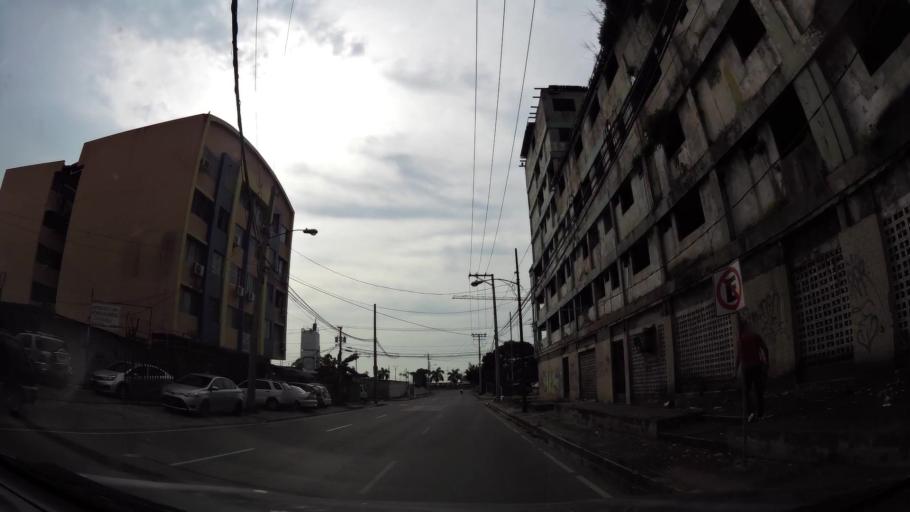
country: PA
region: Panama
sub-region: Distrito de Panama
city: Ancon
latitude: 8.9618
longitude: -79.5381
